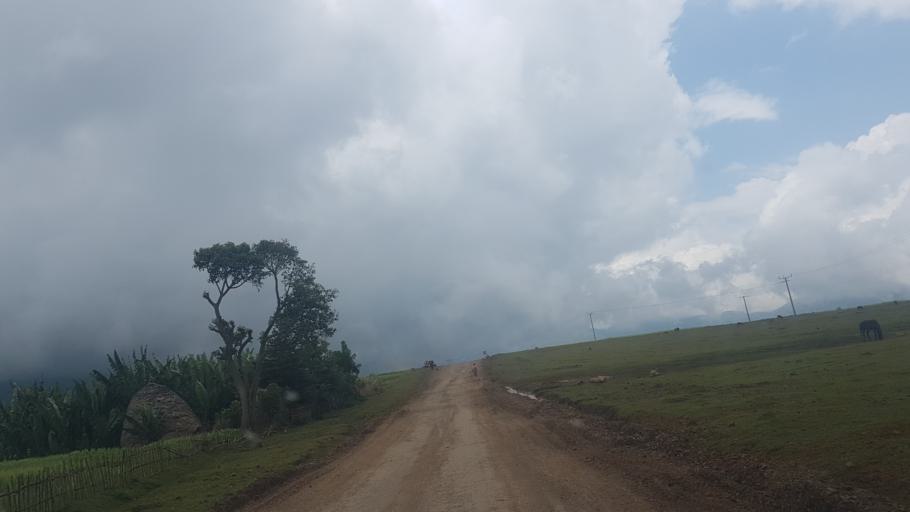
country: ET
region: Southern Nations, Nationalities, and People's Region
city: Arba Minch'
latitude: 6.3242
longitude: 37.5411
